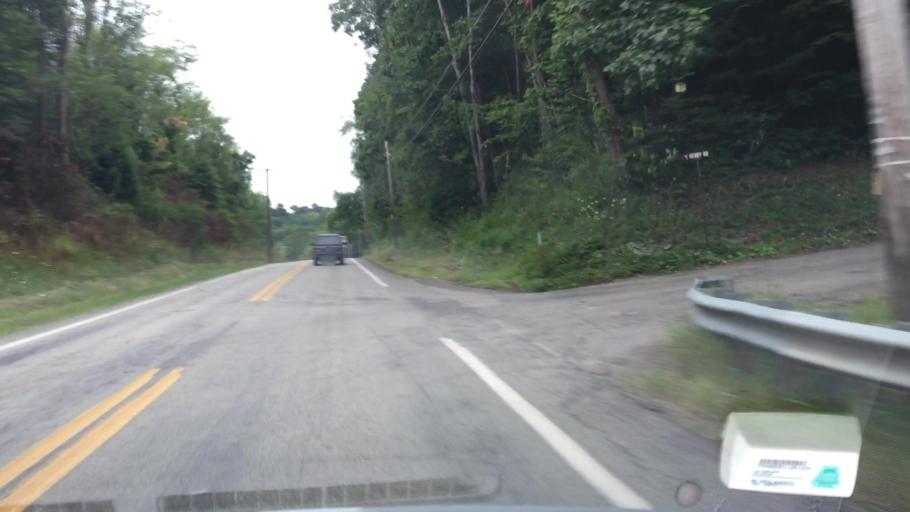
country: US
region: Pennsylvania
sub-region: Allegheny County
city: Curtisville
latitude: 40.6677
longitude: -79.8334
